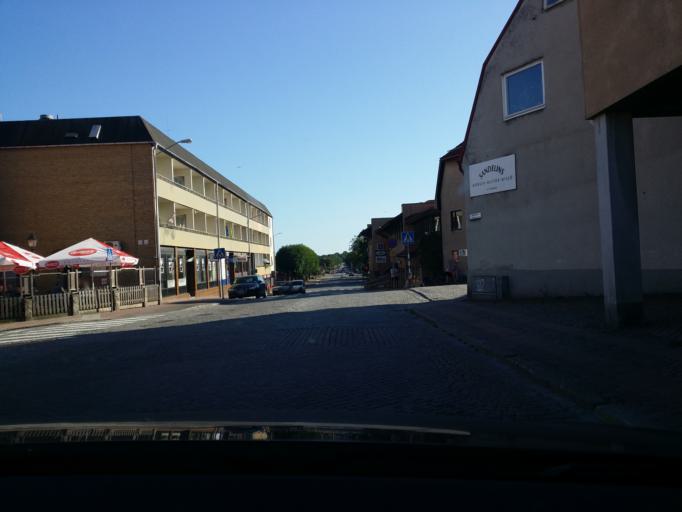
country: SE
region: Blekinge
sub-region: Solvesborgs Kommun
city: Soelvesborg
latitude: 56.0533
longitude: 14.5837
